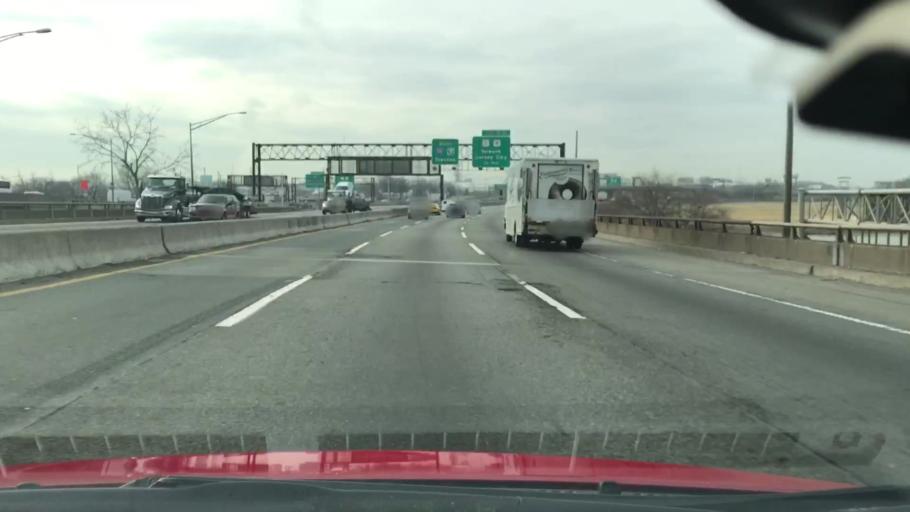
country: US
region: New Jersey
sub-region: Hudson County
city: Harrison
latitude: 40.7366
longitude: -74.1238
